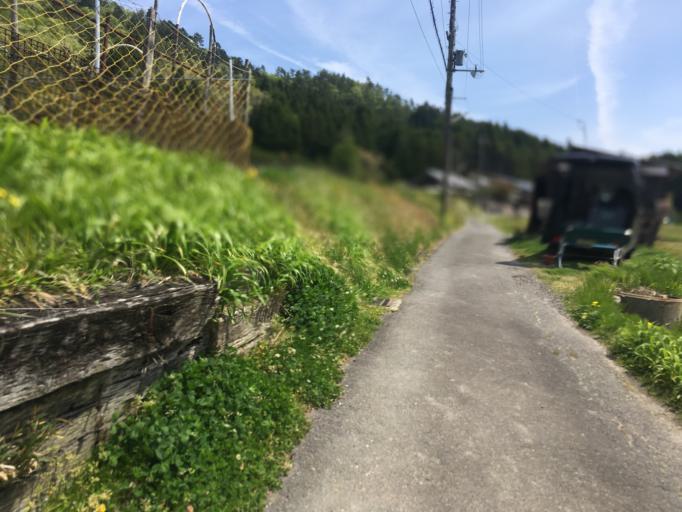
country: JP
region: Kyoto
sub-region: Kyoto-shi
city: Kamigyo-ku
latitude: 35.0849
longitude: 135.7229
